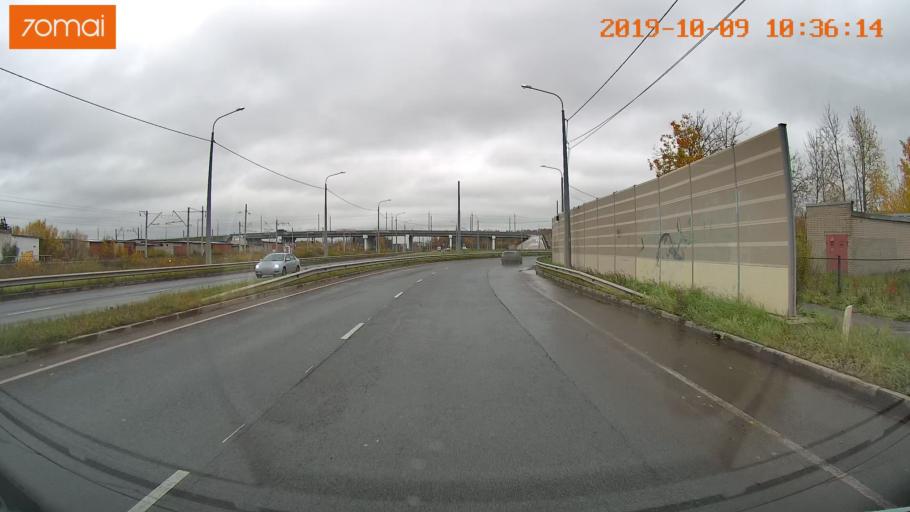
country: RU
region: Vologda
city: Vologda
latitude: 59.2319
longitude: 39.8645
